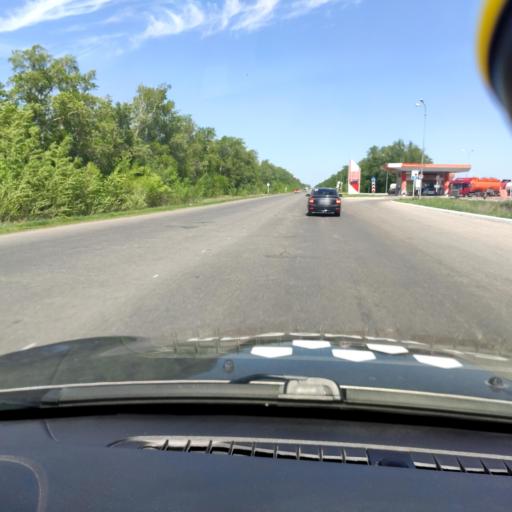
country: RU
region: Samara
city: Tol'yatti
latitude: 53.5953
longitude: 49.4076
